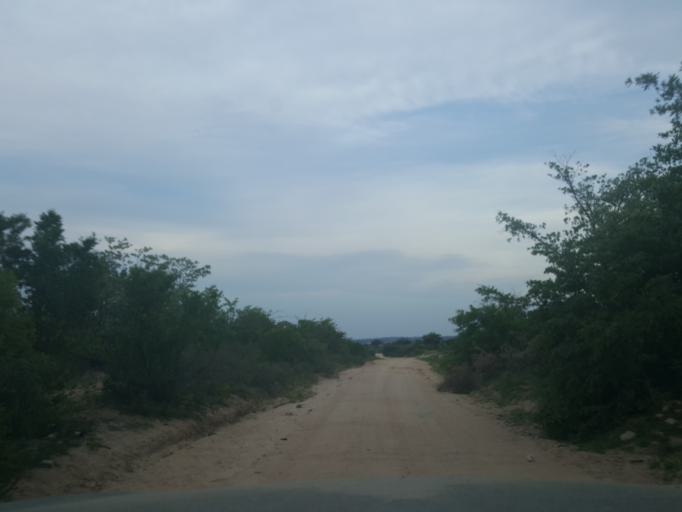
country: ZA
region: Limpopo
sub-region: Mopani District Municipality
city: Hoedspruit
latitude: -24.5844
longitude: 30.9815
